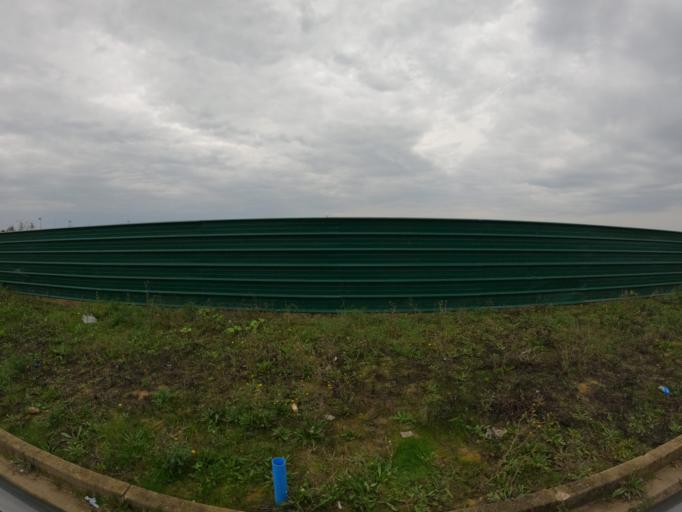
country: FR
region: Ile-de-France
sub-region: Departement de Seine-et-Marne
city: Serris
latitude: 48.8377
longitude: 2.8007
